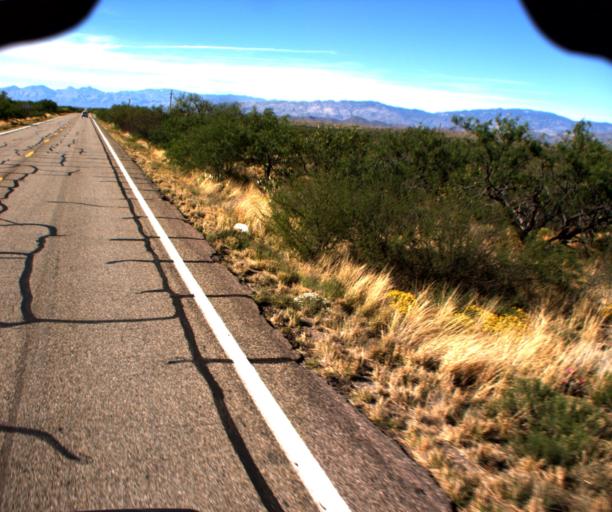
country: US
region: Arizona
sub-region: Pima County
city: Corona de Tucson
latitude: 31.9437
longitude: -110.6640
